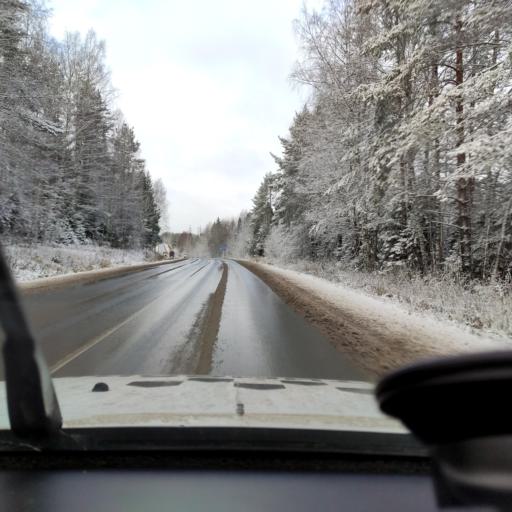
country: RU
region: Perm
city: Nytva
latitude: 57.9314
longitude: 55.3886
